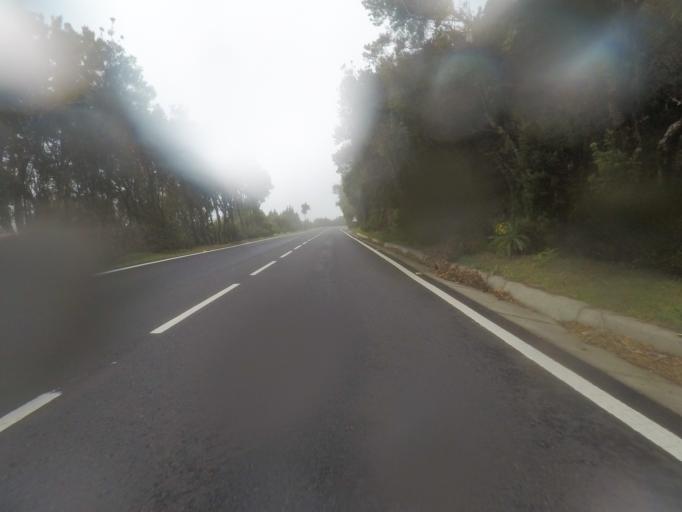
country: ES
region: Canary Islands
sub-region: Provincia de Santa Cruz de Tenerife
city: Vallehermosa
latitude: 28.1273
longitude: -17.2670
